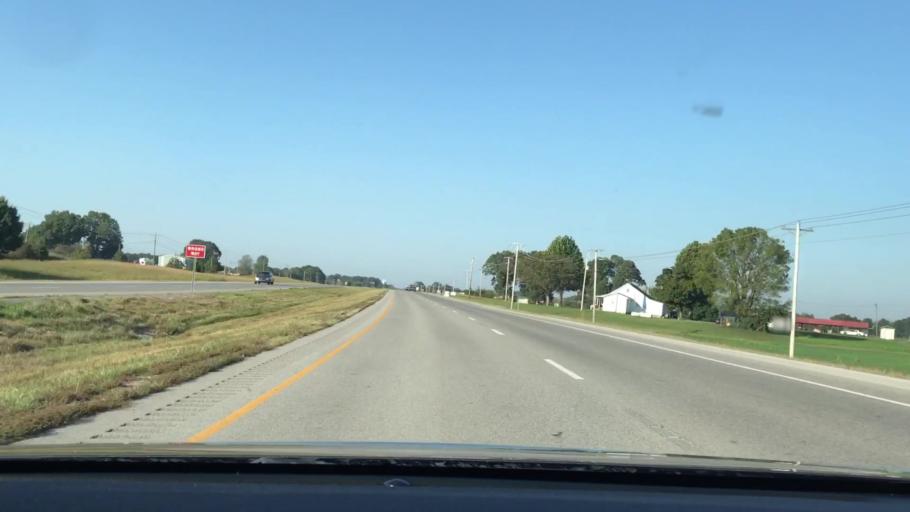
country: US
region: Kentucky
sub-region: Trigg County
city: Cadiz
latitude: 36.8762
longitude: -87.7520
